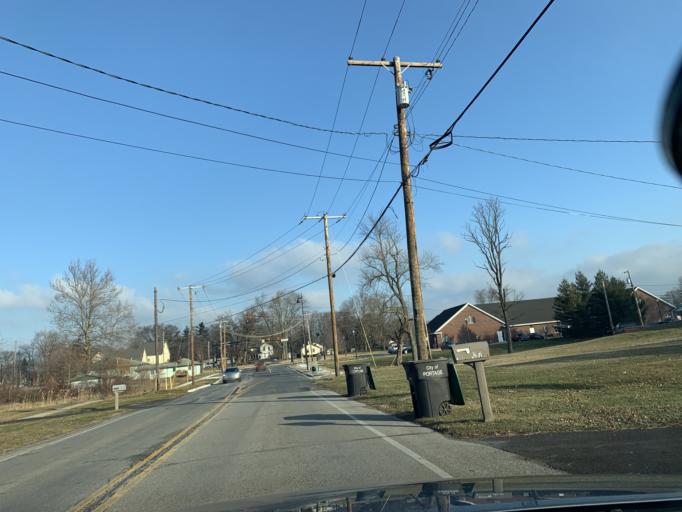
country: US
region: Indiana
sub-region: Porter County
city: Portage
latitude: 41.5745
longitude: -87.1637
